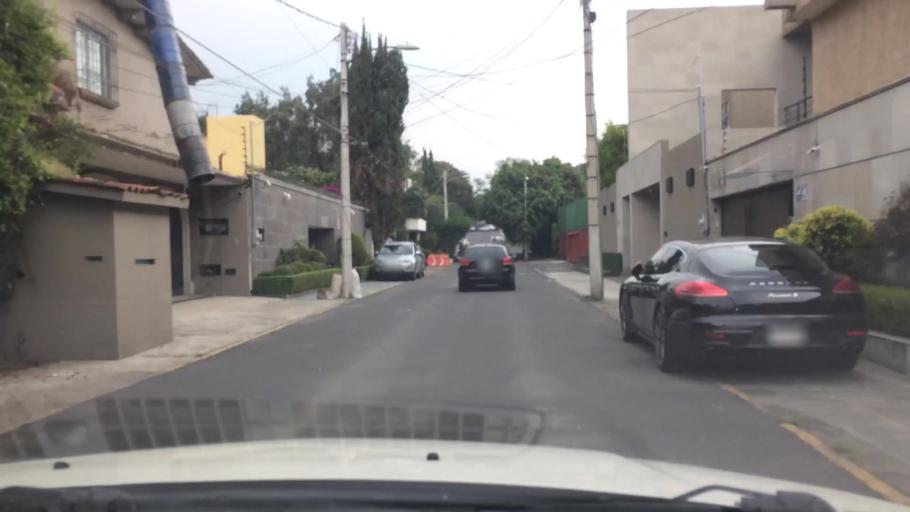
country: MX
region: Mexico City
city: Magdalena Contreras
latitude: 19.3149
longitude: -99.2104
